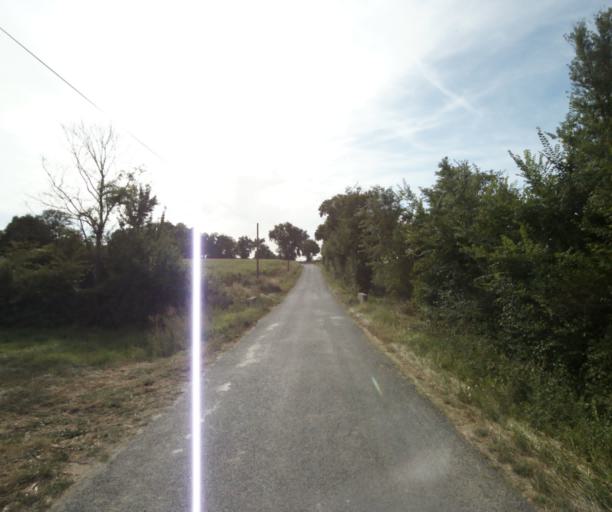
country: FR
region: Midi-Pyrenees
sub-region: Departement du Tarn
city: Puylaurens
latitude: 43.5251
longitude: 2.0362
